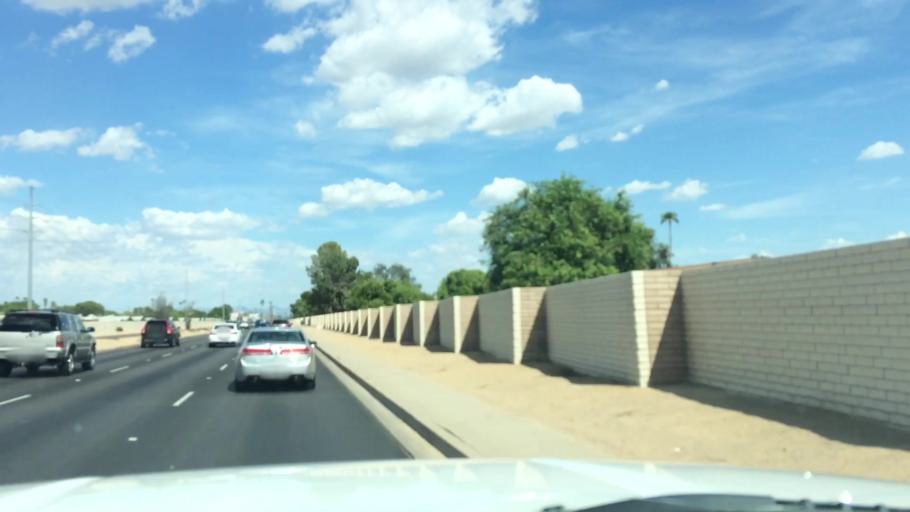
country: US
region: Arizona
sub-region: Maricopa County
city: Sun City
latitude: 33.6388
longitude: -112.2871
